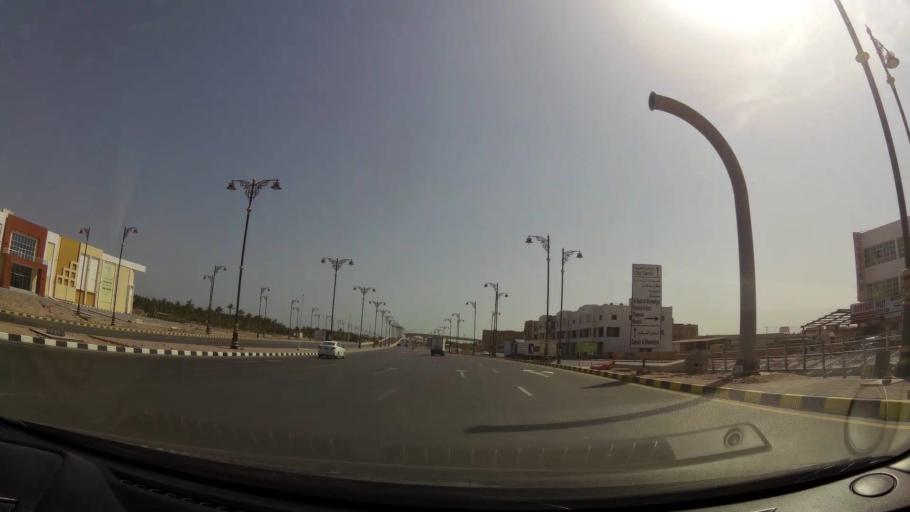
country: OM
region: Zufar
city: Salalah
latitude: 17.0360
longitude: 54.1478
